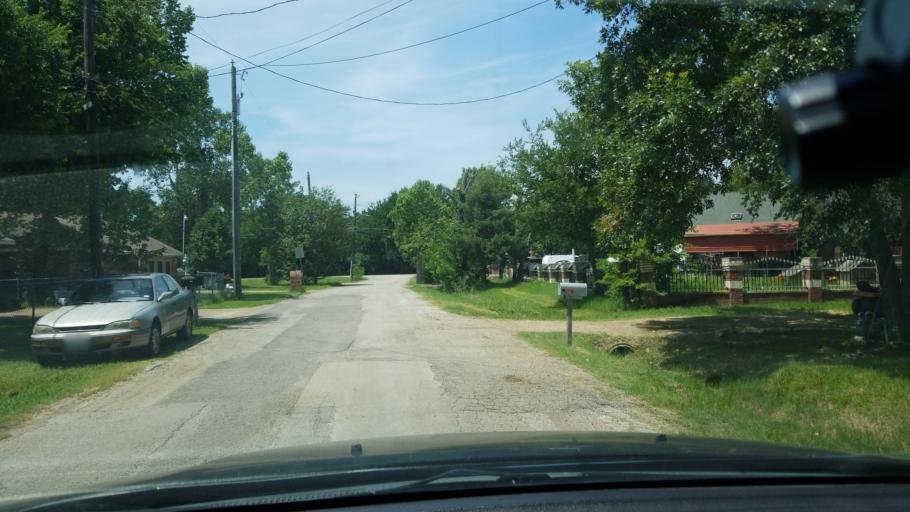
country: US
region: Texas
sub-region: Dallas County
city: Balch Springs
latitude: 32.7526
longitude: -96.6342
